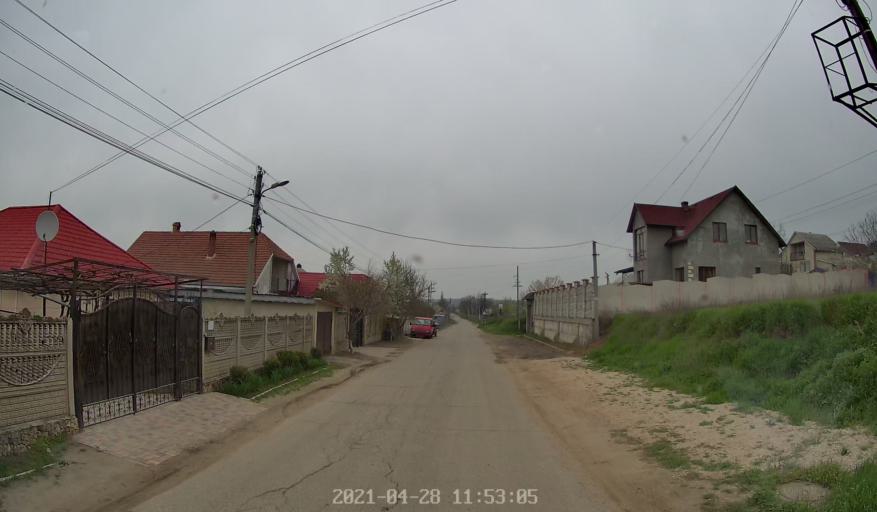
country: MD
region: Chisinau
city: Singera
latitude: 46.9522
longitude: 28.9429
